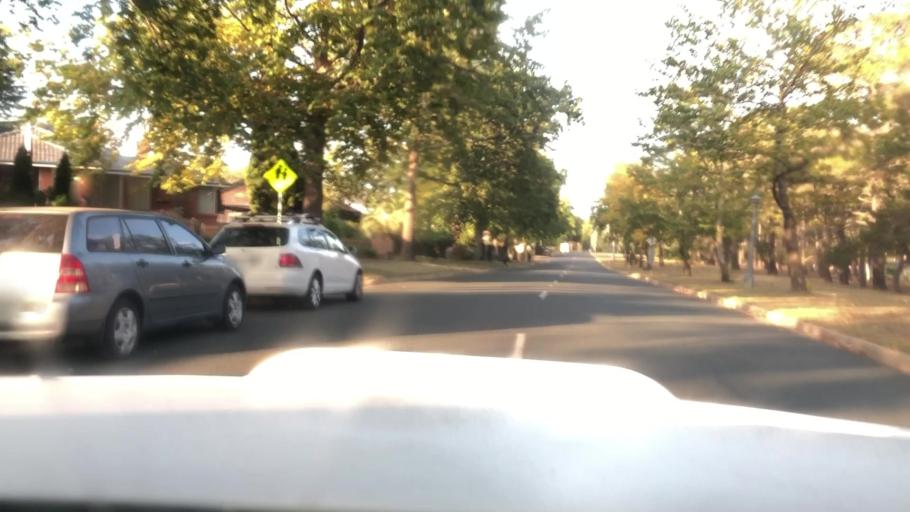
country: AU
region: Australian Capital Territory
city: Canberra
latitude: -35.2515
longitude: 149.1634
